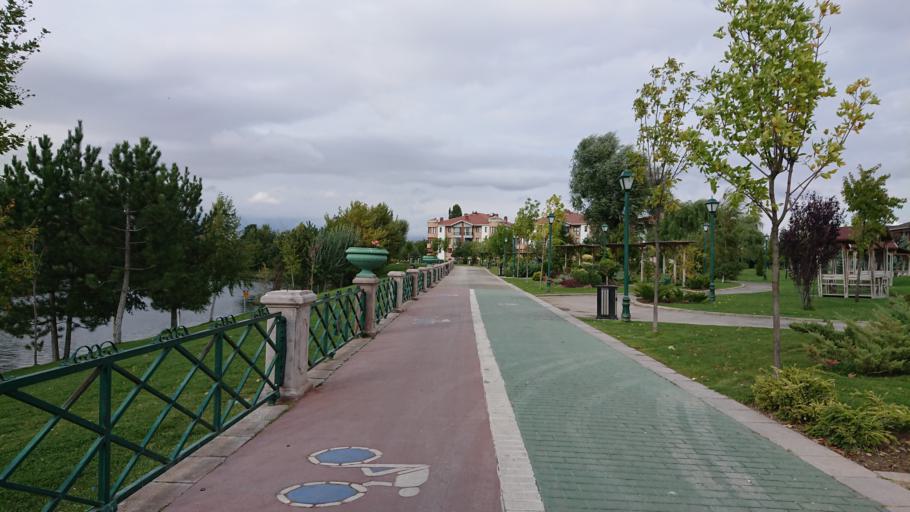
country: TR
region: Eskisehir
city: Eskisehir
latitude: 39.7622
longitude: 30.4860
